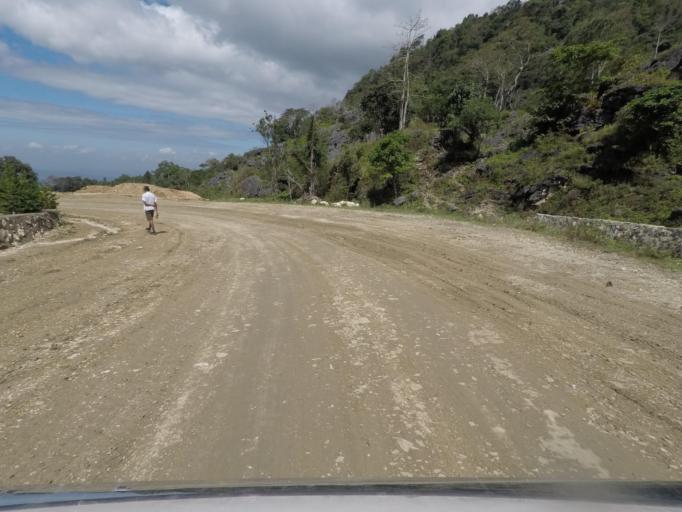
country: TL
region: Baucau
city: Venilale
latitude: -8.7298
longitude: 126.3682
